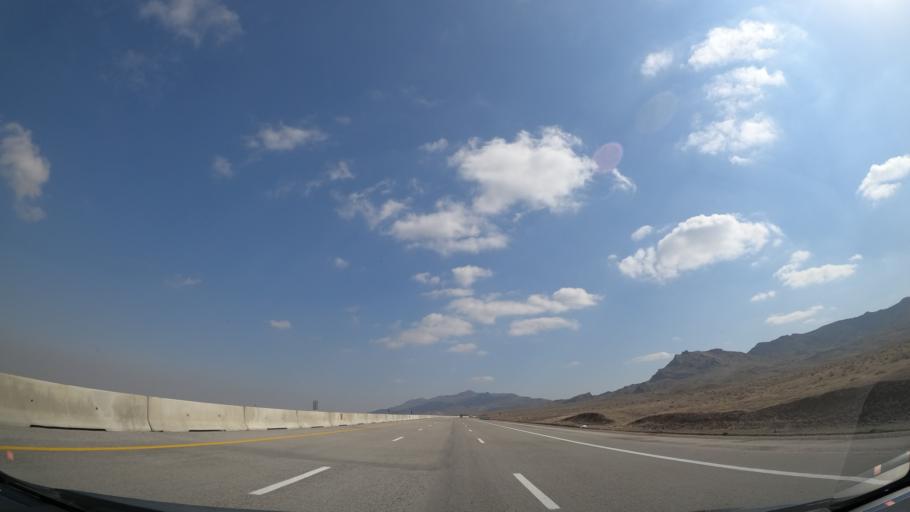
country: IR
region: Alborz
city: Eshtehard
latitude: 35.7079
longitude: 50.6040
